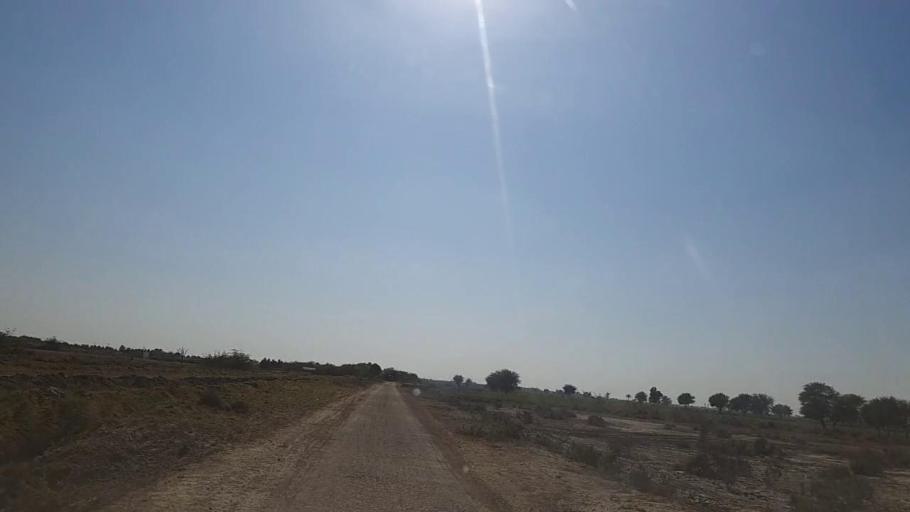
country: PK
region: Sindh
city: Digri
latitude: 25.1180
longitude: 69.0487
